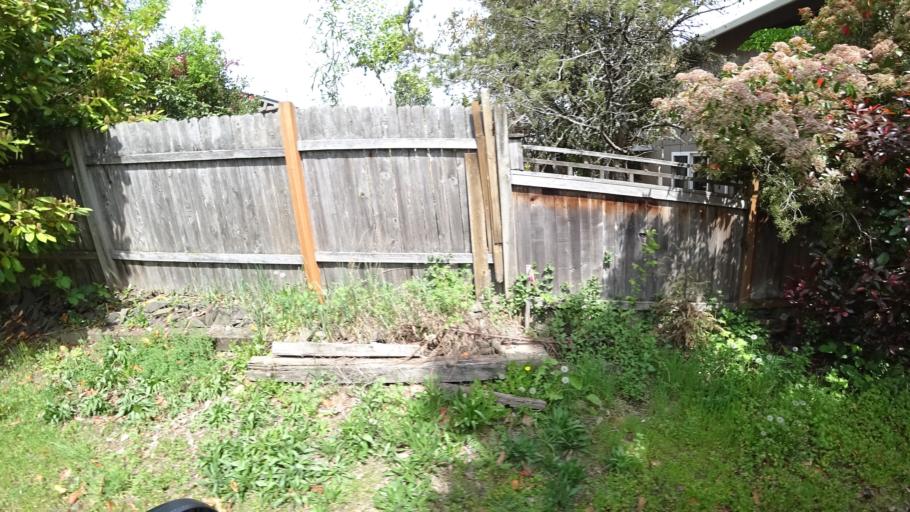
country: US
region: Oregon
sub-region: Washington County
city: Aloha
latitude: 45.4584
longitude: -122.8460
